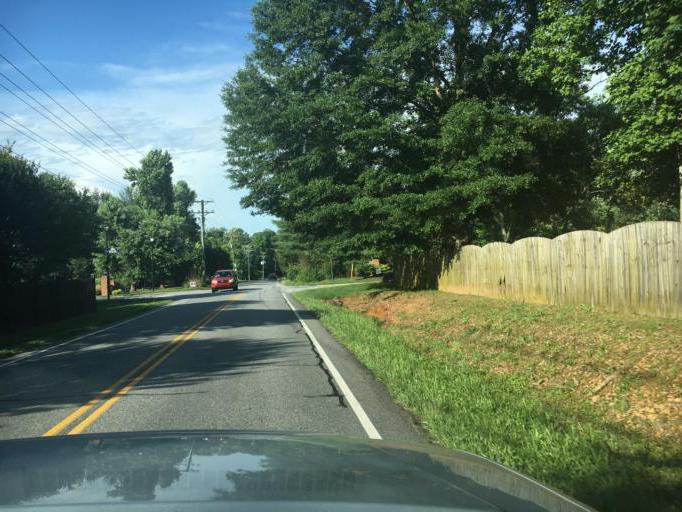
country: US
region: South Carolina
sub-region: Greenville County
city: Five Forks
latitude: 34.7872
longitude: -82.2395
